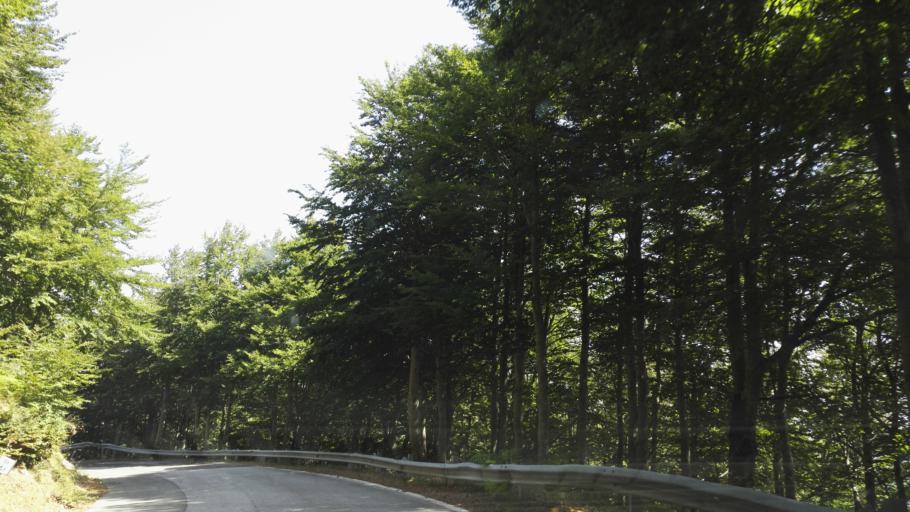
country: IT
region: Calabria
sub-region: Provincia di Vibo-Valentia
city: Nardodipace
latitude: 38.5083
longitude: 16.3558
